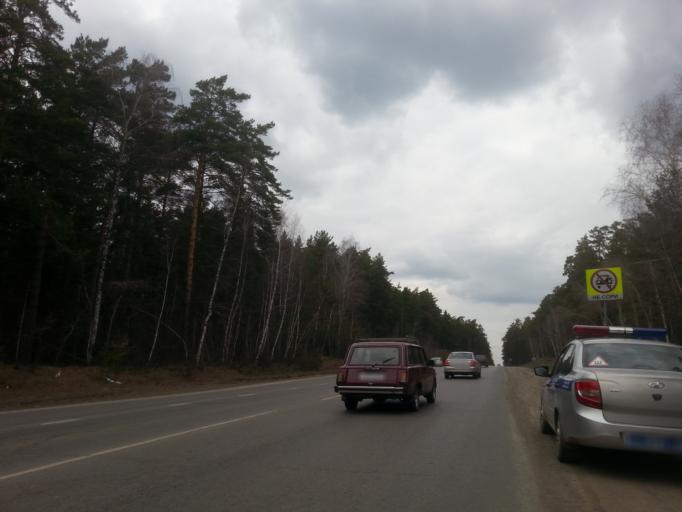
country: RU
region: Altai Krai
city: Yuzhnyy
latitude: 53.2691
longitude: 83.7258
